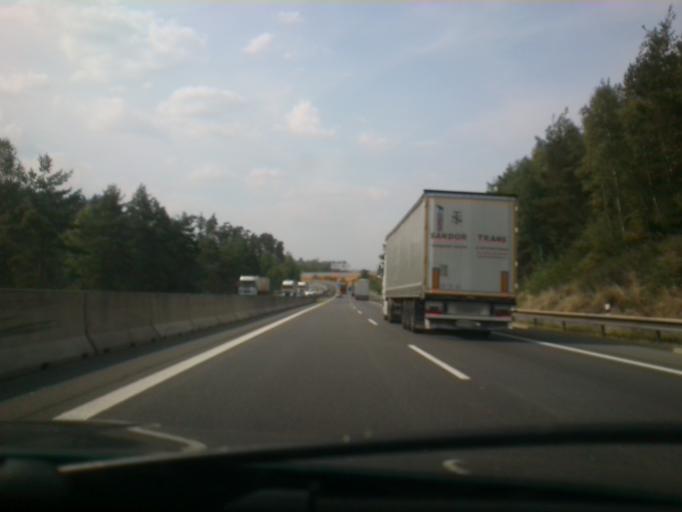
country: CZ
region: Central Bohemia
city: Trhovy Stepanov
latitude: 49.7467
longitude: 15.0298
